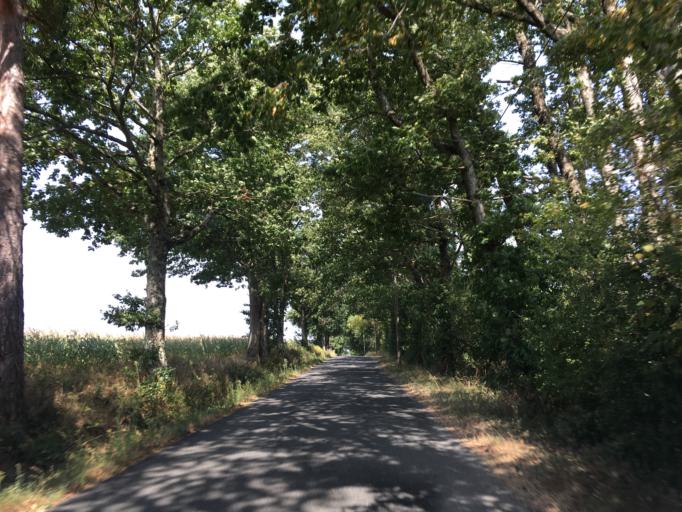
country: FR
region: Midi-Pyrenees
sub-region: Departement du Tarn
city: Lagarrigue
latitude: 43.6059
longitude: 2.2971
